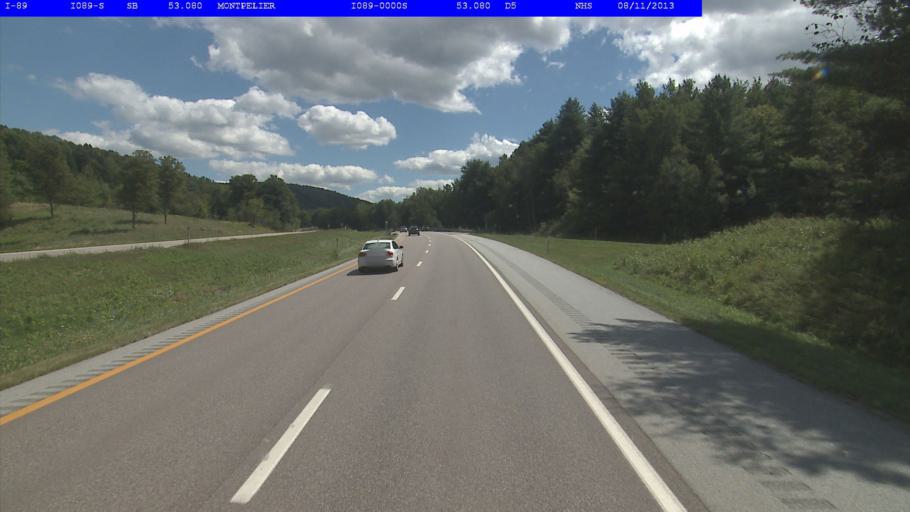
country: US
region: Vermont
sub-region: Washington County
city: Montpelier
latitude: 44.2519
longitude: -72.5973
